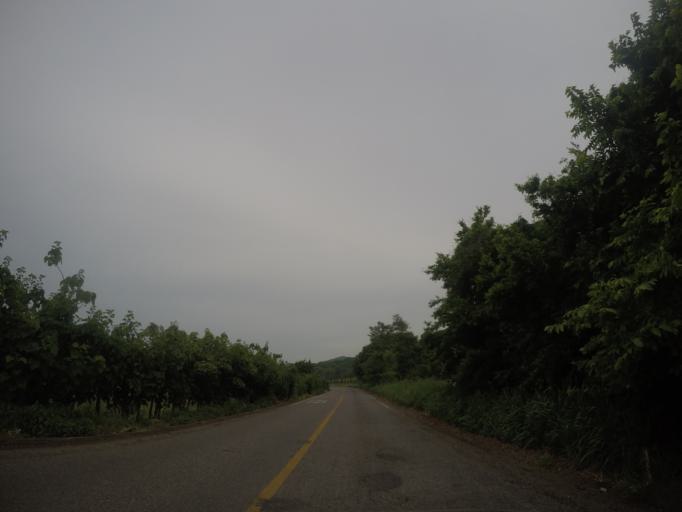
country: MX
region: Oaxaca
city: San Pedro Mixtepec
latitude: 15.9544
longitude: -97.2001
